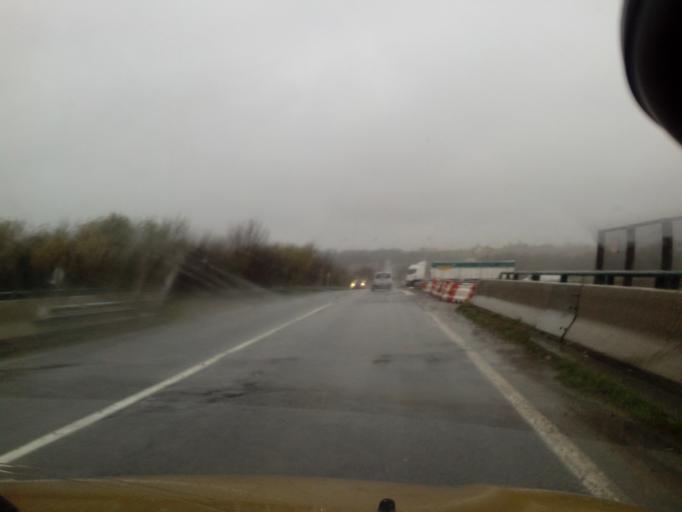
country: FR
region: Brittany
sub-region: Departement d'Ille-et-Vilaine
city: Montauban-de-Bretagne
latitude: 48.2022
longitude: -2.0824
